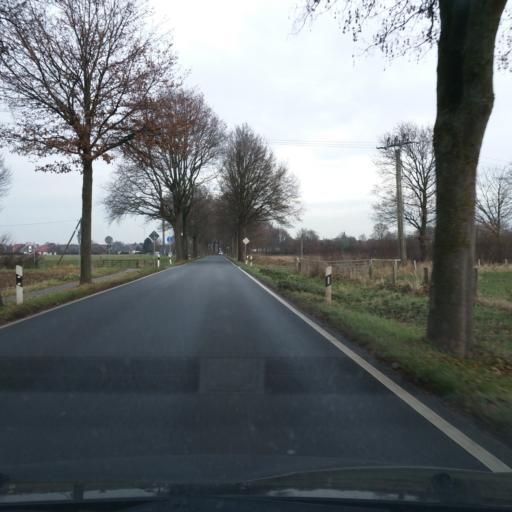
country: DE
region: North Rhine-Westphalia
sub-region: Regierungsbezirk Munster
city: Isselburg
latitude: 51.8135
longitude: 6.5032
